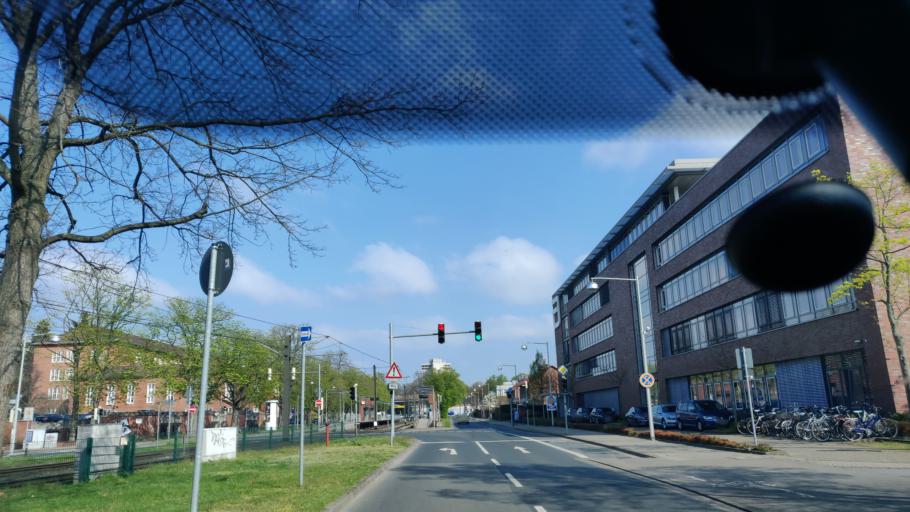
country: DE
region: Lower Saxony
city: Hannover
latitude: 52.3683
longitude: 9.7721
